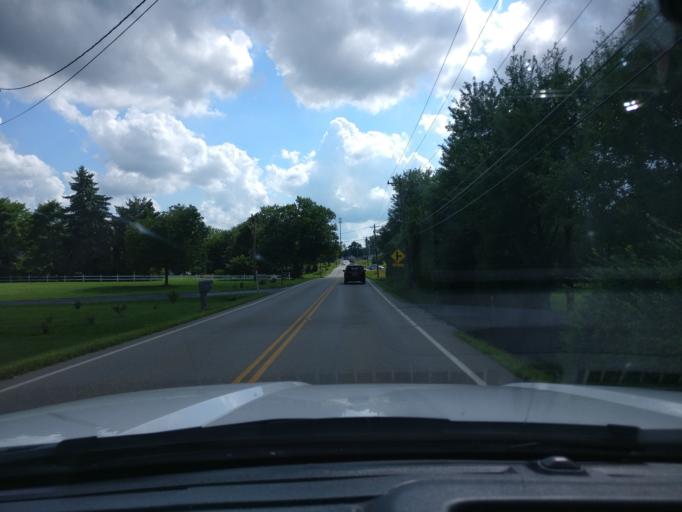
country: US
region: Ohio
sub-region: Warren County
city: Springboro
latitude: 39.5063
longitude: -84.1961
